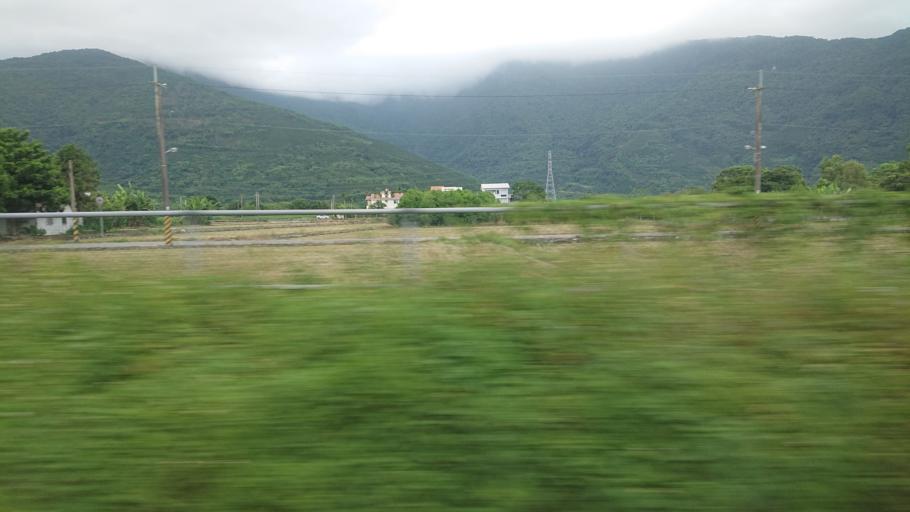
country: TW
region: Taiwan
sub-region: Hualien
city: Hualian
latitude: 23.7436
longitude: 121.4453
